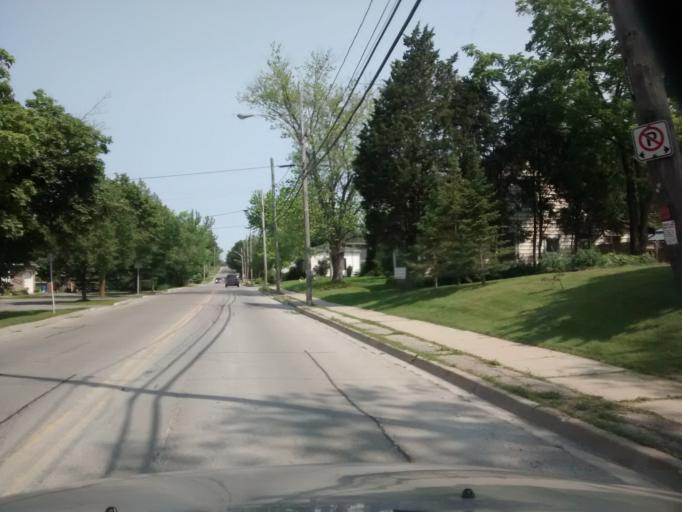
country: CA
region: Ontario
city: Ancaster
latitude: 42.9514
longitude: -79.8562
